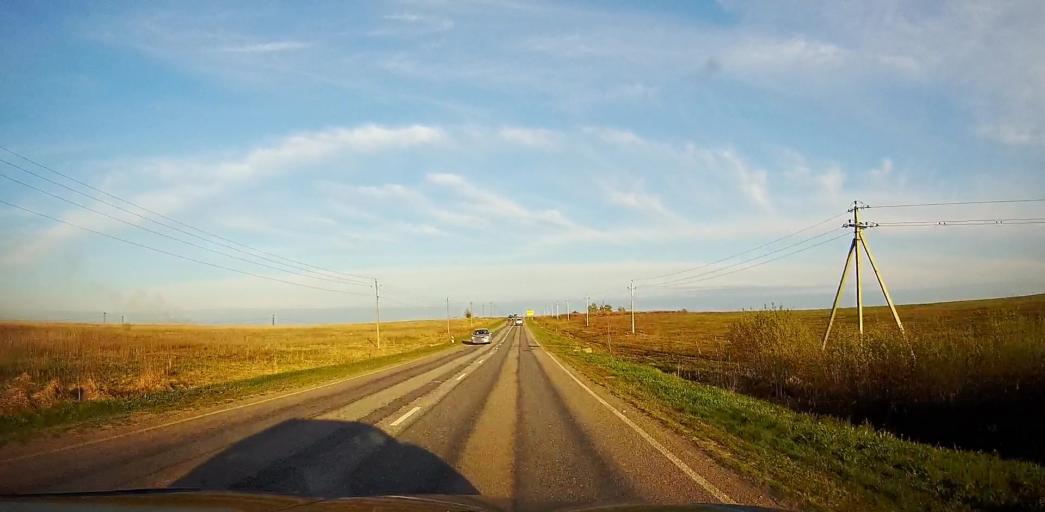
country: RU
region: Moskovskaya
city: Meshcherino
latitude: 55.2698
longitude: 38.2419
